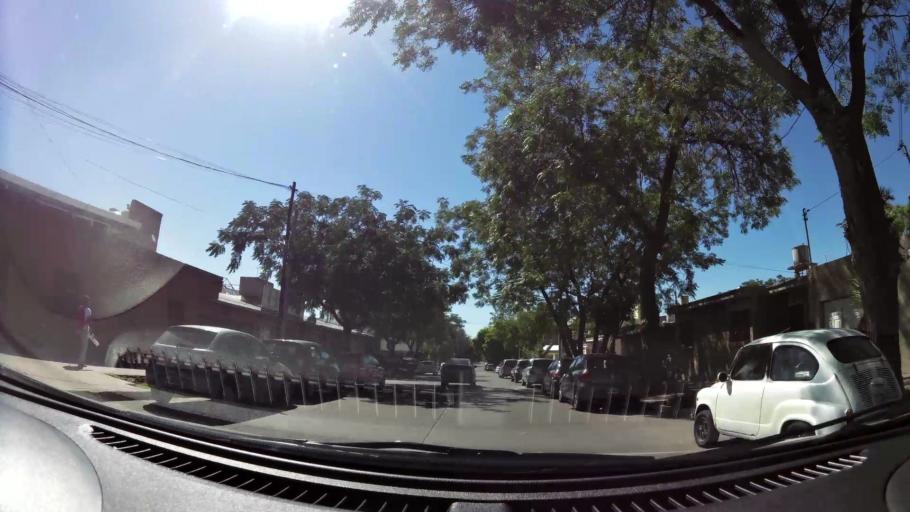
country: AR
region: Mendoza
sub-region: Departamento de Godoy Cruz
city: Godoy Cruz
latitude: -32.9067
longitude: -68.8618
